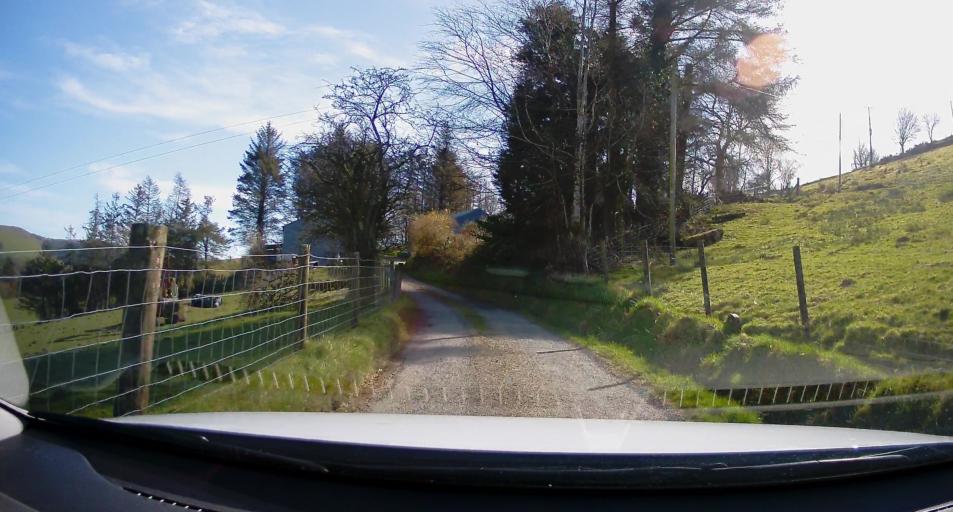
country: GB
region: Wales
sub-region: County of Ceredigion
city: Lledrod
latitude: 52.3690
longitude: -3.8669
